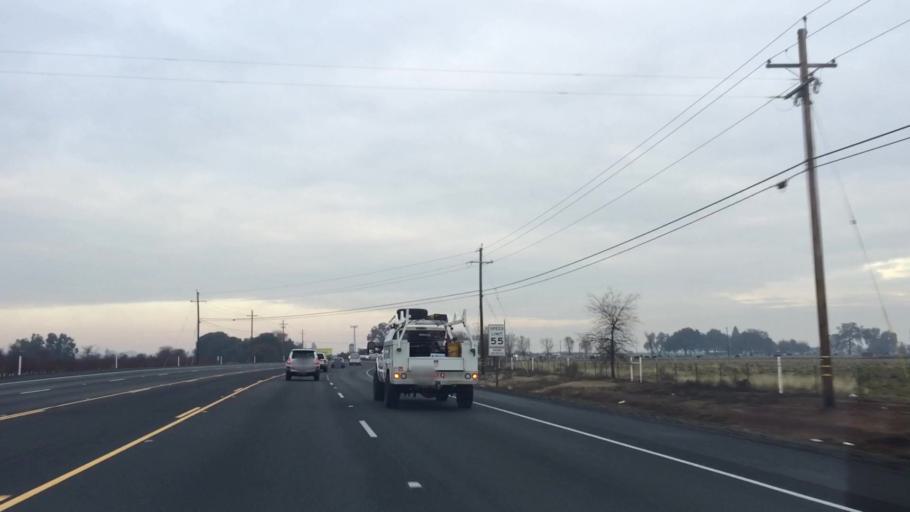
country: US
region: California
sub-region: Butte County
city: Gridley
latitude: 39.3767
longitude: -121.6126
